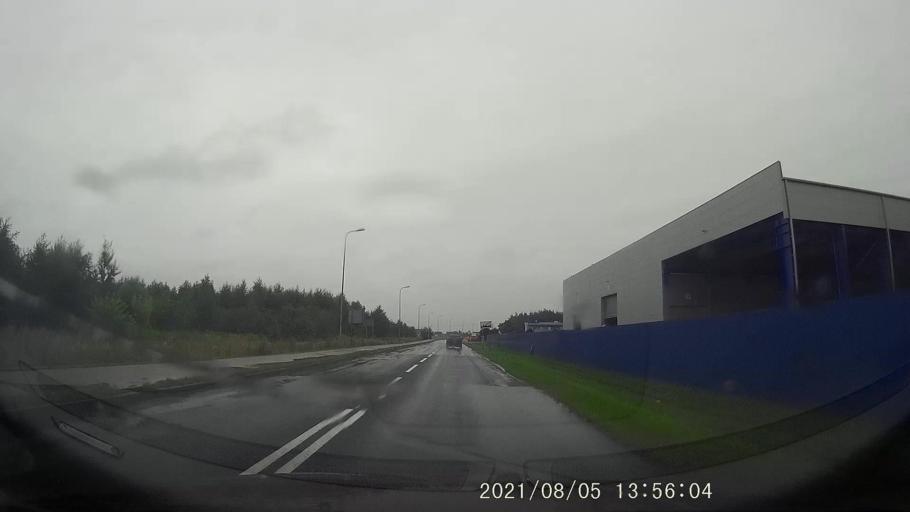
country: PL
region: Opole Voivodeship
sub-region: Powiat krapkowicki
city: Krapkowice
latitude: 50.4655
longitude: 17.9483
